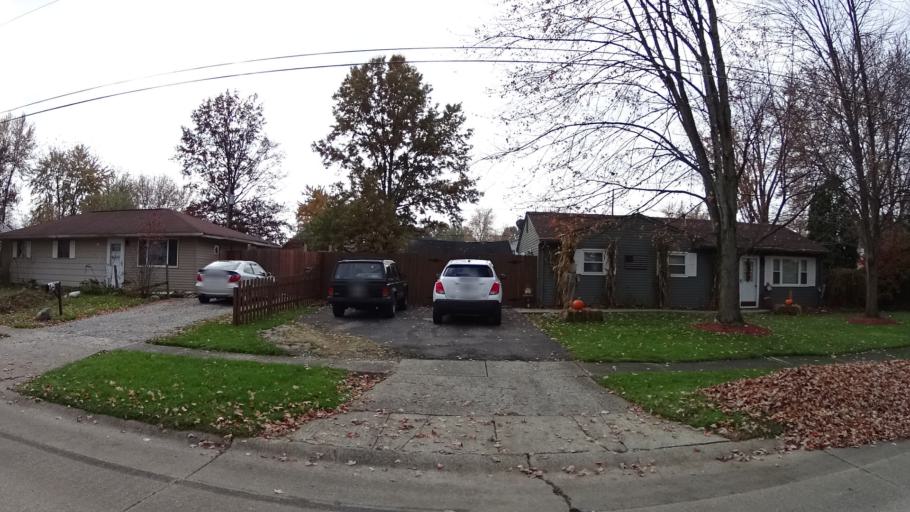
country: US
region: Ohio
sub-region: Lorain County
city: Elyria
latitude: 41.3561
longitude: -82.0801
